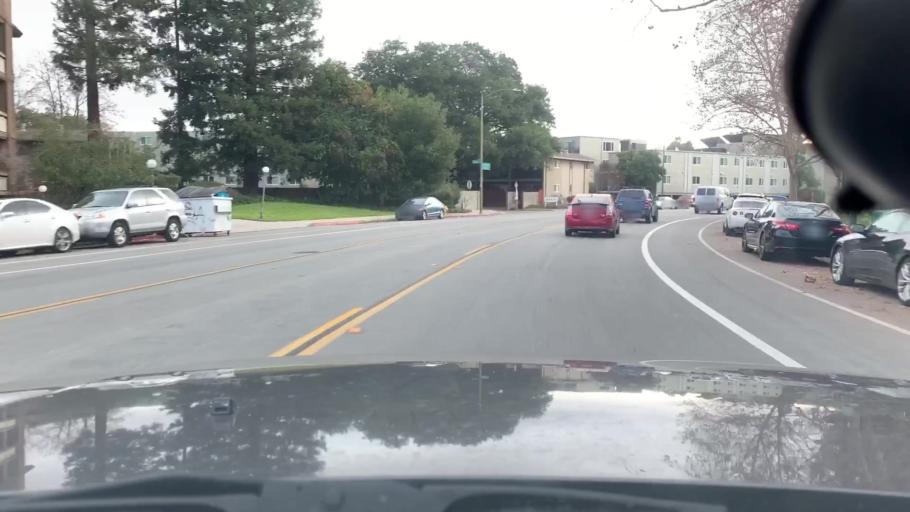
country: US
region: California
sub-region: Santa Clara County
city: Campbell
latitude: 37.3026
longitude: -121.9777
